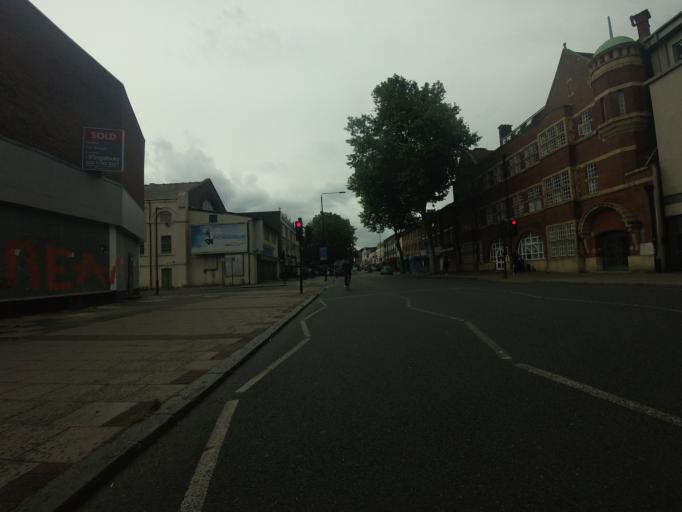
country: GB
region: England
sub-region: Greater London
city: East Ham
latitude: 51.5211
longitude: 0.0199
